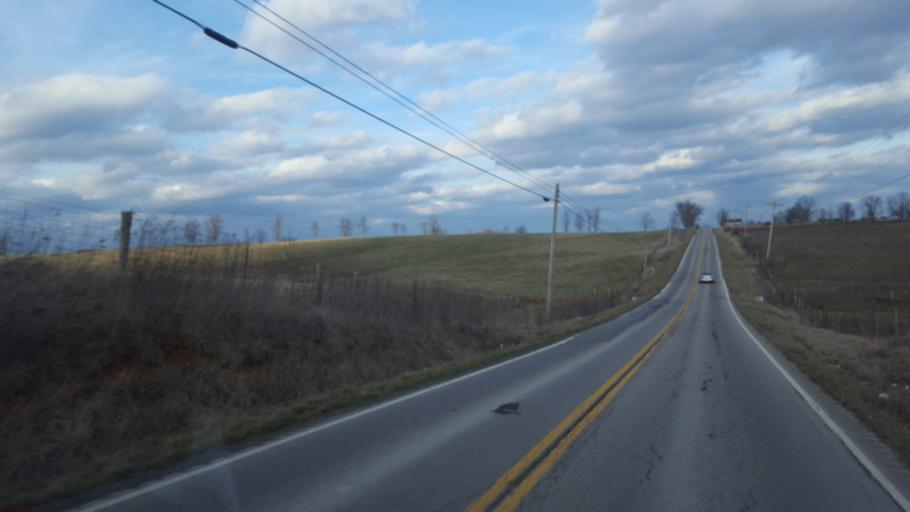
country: US
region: Kentucky
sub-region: Fleming County
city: Flemingsburg
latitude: 38.4747
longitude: -83.6637
